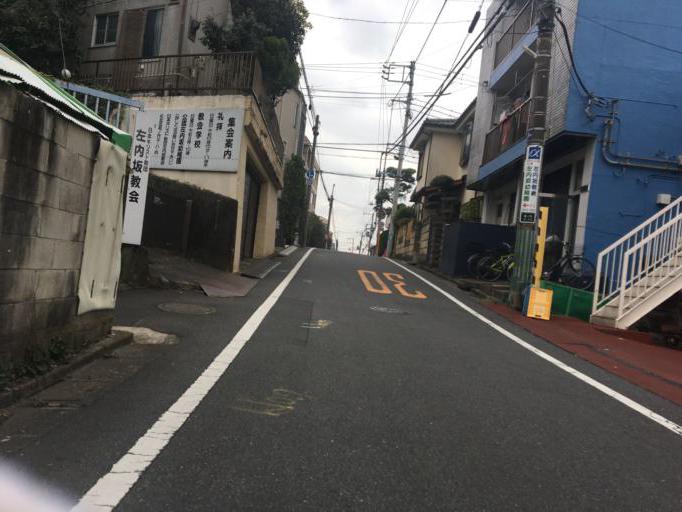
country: JP
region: Tokyo
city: Tokyo
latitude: 35.6906
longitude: 139.6506
